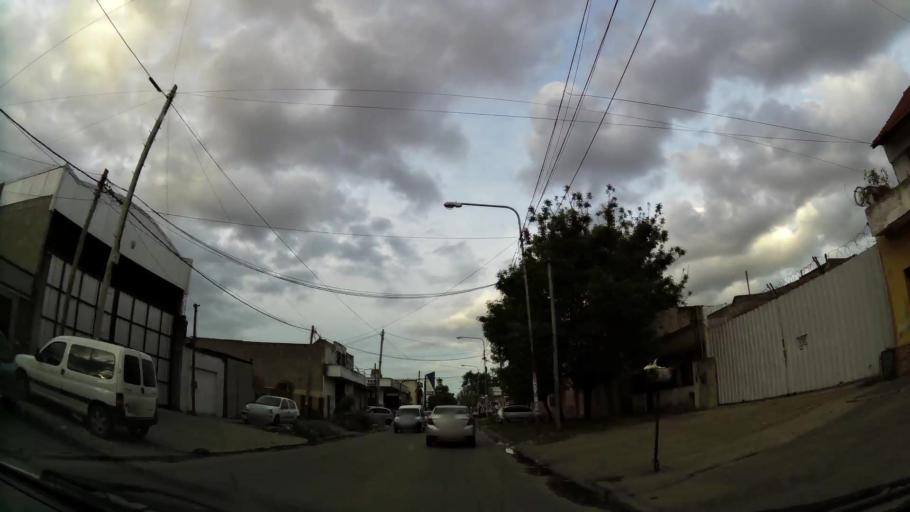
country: AR
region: Buenos Aires
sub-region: Partido de Quilmes
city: Quilmes
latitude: -34.7525
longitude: -58.2274
